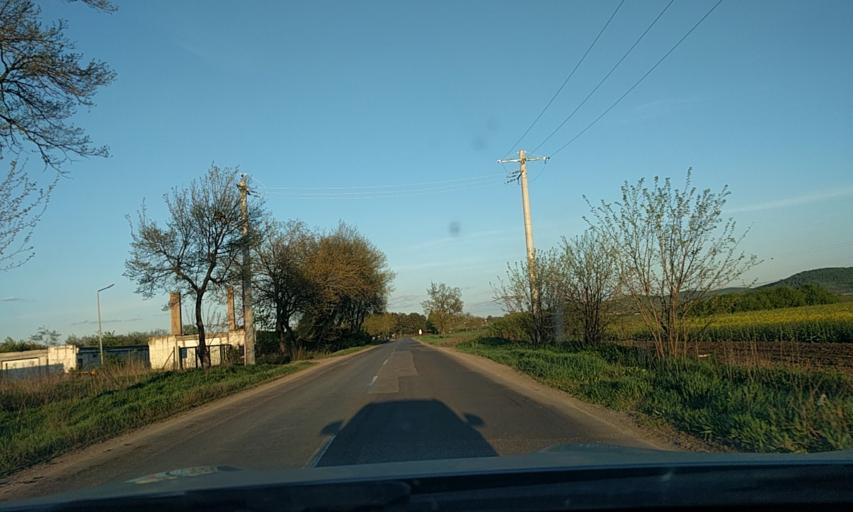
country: RO
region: Mures
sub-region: Comuna Ungheni
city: Ungheni
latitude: 46.4762
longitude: 24.4684
